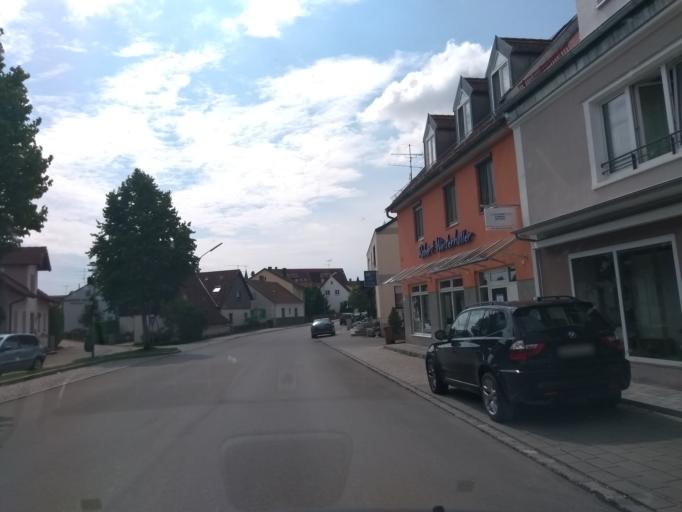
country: DE
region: Bavaria
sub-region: Upper Bavaria
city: Markt Indersdorf
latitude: 48.3629
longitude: 11.3765
